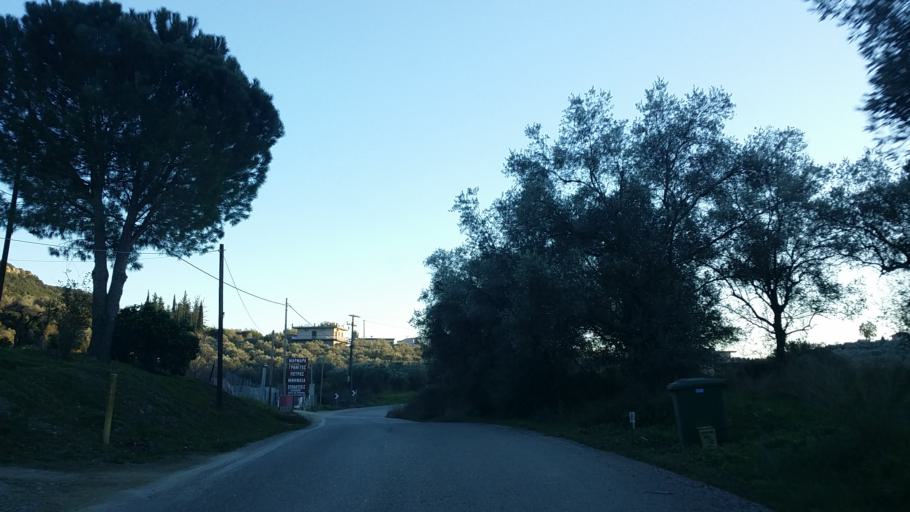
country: GR
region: West Greece
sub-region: Nomos Aitolias kai Akarnanias
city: Neapolis
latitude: 38.6975
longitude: 21.3532
